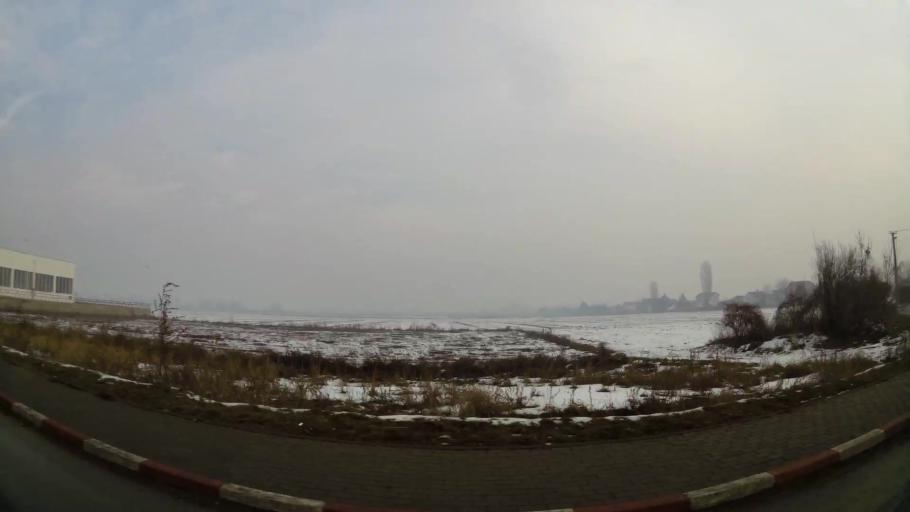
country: MK
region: Ilinden
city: Jurumleri
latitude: 41.9773
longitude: 21.5332
